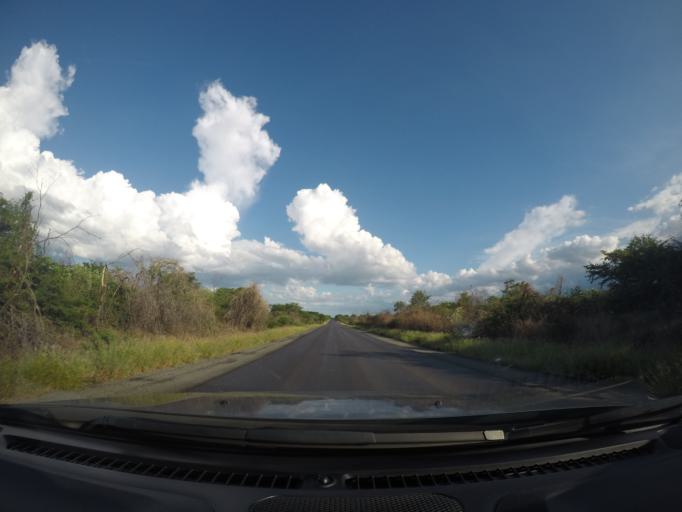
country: BR
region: Bahia
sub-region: Oliveira Dos Brejinhos
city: Oliveira dos Brejinhos
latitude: -12.0864
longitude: -42.9364
